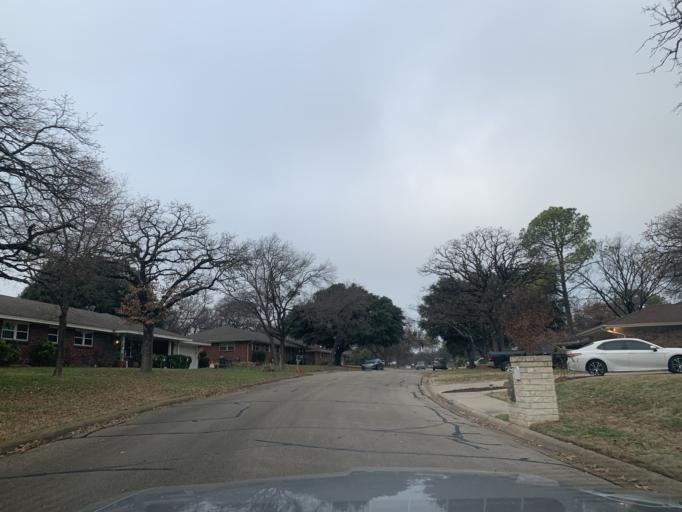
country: US
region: Texas
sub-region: Tarrant County
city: Bedford
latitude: 32.8307
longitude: -97.1520
